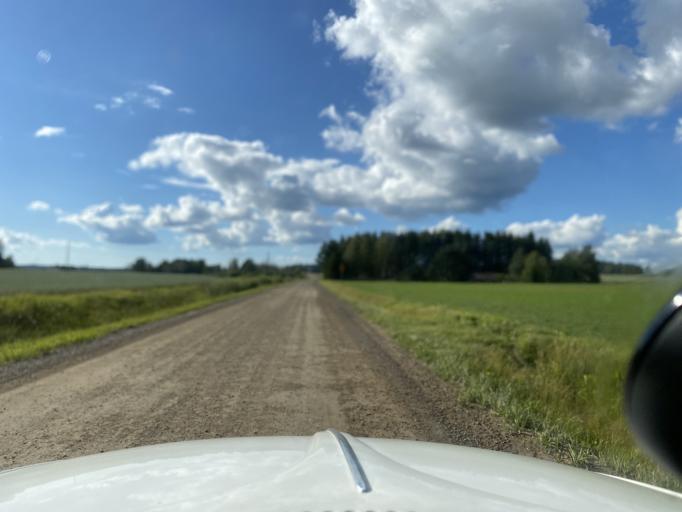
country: FI
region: Pirkanmaa
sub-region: Lounais-Pirkanmaa
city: Punkalaidun
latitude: 61.1306
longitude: 23.2397
